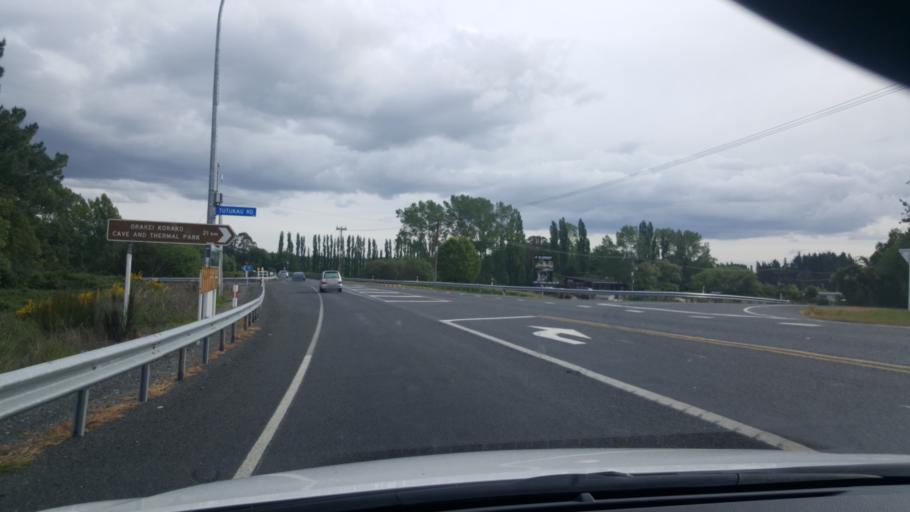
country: NZ
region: Waikato
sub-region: Taupo District
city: Taupo
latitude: -38.4836
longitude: 176.2915
